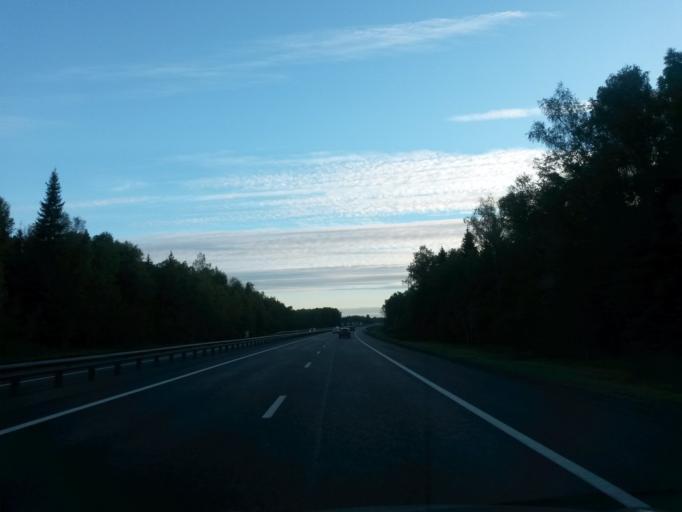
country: RU
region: Moskovskaya
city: Svatkovo
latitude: 56.4145
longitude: 38.3296
